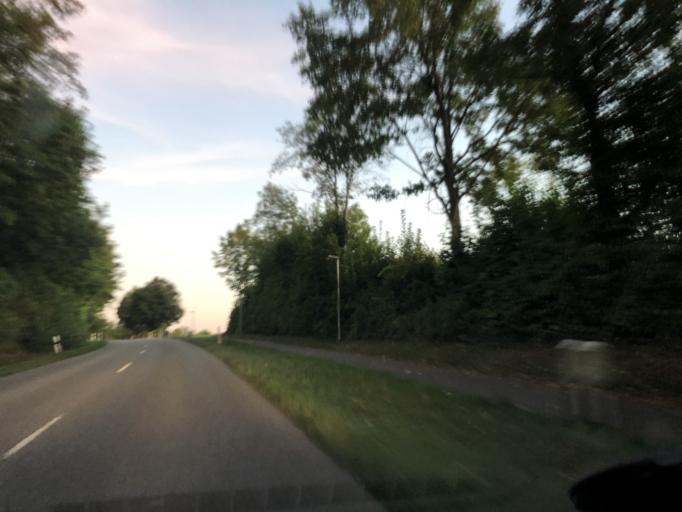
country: DE
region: Baden-Wuerttemberg
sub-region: Regierungsbezirk Stuttgart
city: Erdmannhausen
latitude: 48.8830
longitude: 9.2799
